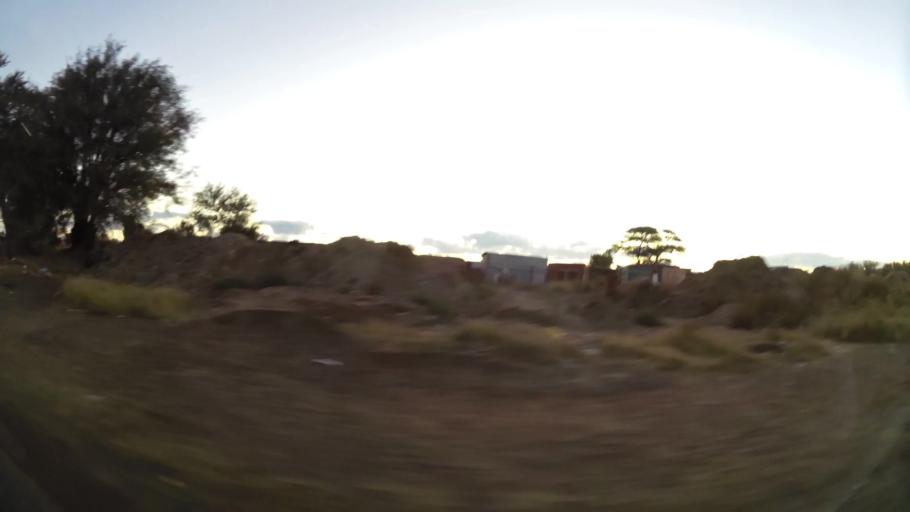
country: ZA
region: Northern Cape
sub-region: Frances Baard District Municipality
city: Kimberley
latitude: -28.7214
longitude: 24.7625
